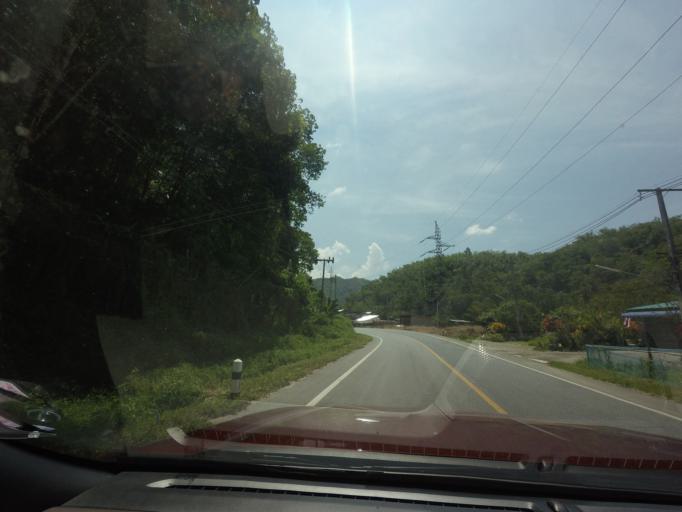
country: TH
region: Yala
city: Betong
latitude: 5.8262
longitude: 101.1122
